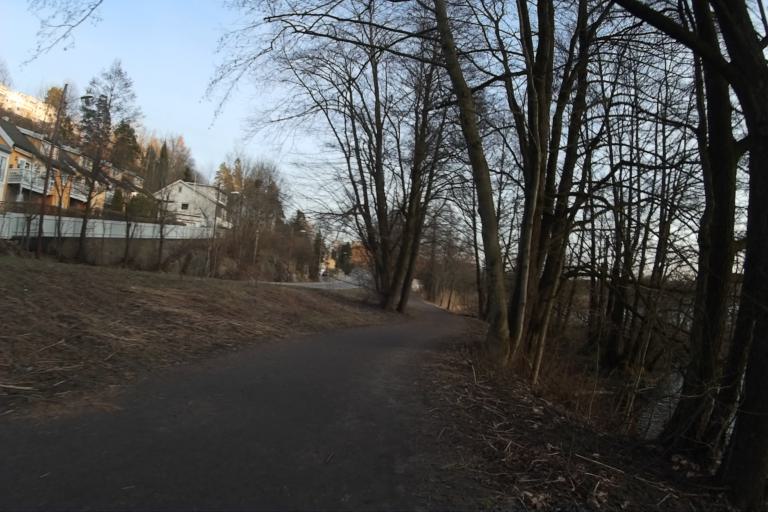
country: NO
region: Akershus
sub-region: Oppegard
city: Kolbotn
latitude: 59.8932
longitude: 10.8328
